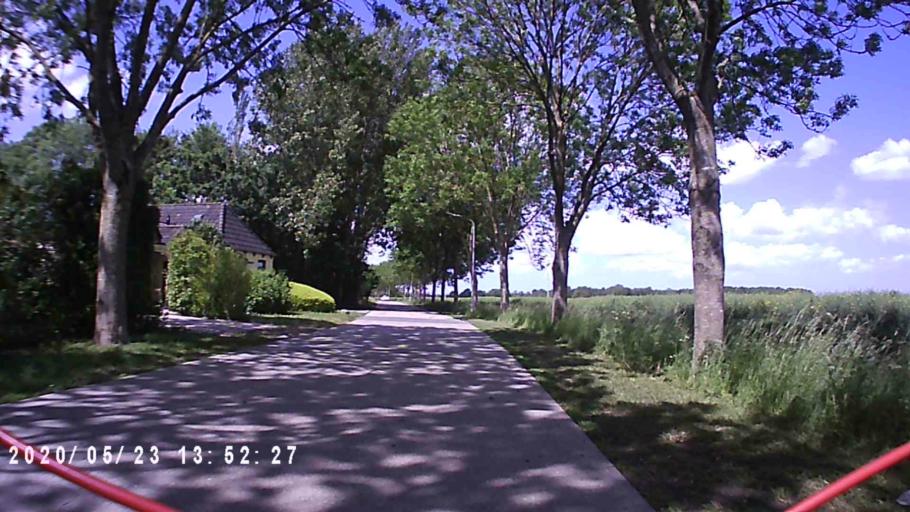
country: NL
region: Groningen
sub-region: Gemeente  Oldambt
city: Winschoten
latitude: 53.2680
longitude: 7.0381
